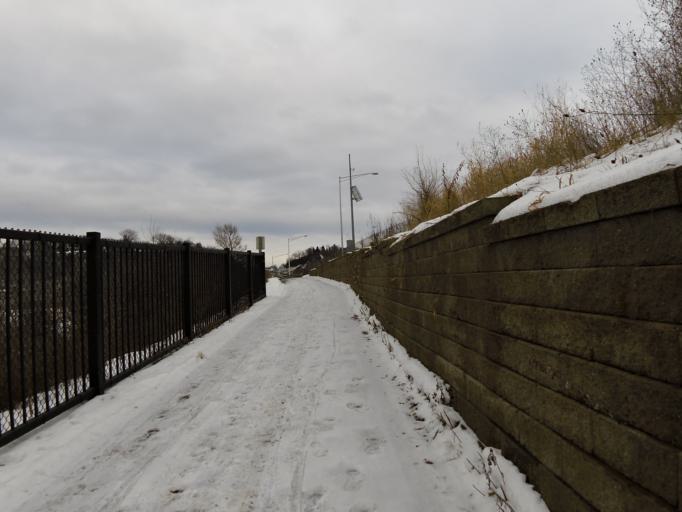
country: US
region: Minnesota
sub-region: Washington County
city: Lakeland
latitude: 44.9631
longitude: -92.7584
